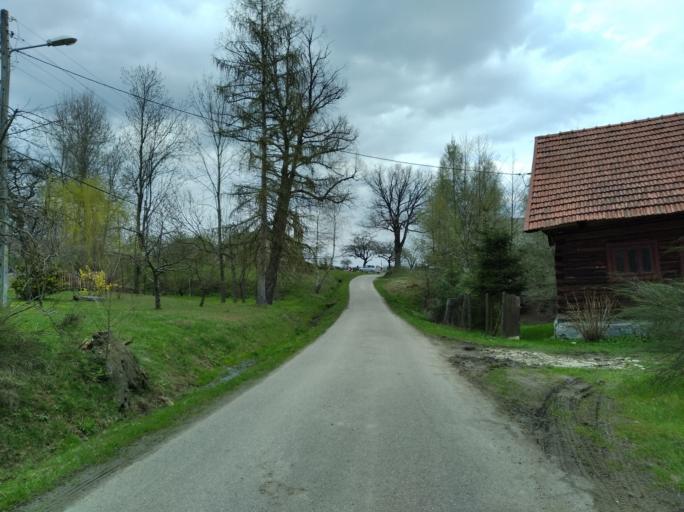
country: PL
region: Subcarpathian Voivodeship
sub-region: Powiat strzyzowski
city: Wysoka Strzyzowska
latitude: 49.8307
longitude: 21.7054
